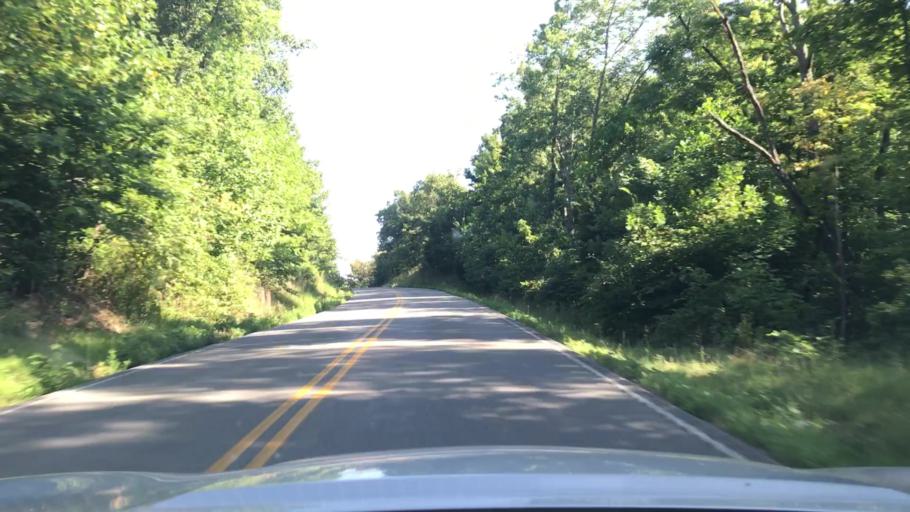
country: US
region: Kentucky
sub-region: Muhlenberg County
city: Greenville
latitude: 37.1124
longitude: -87.1277
